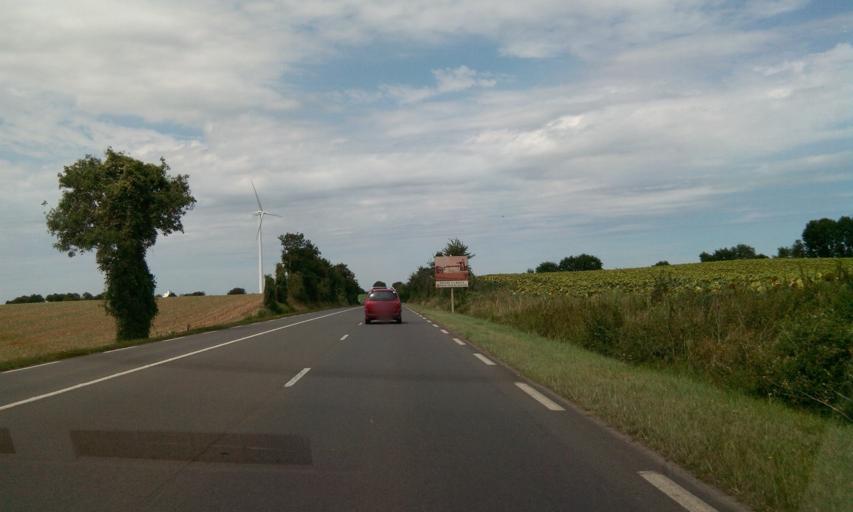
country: FR
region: Poitou-Charentes
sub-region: Departement des Deux-Sevres
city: Melle
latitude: 46.2345
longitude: -0.1691
